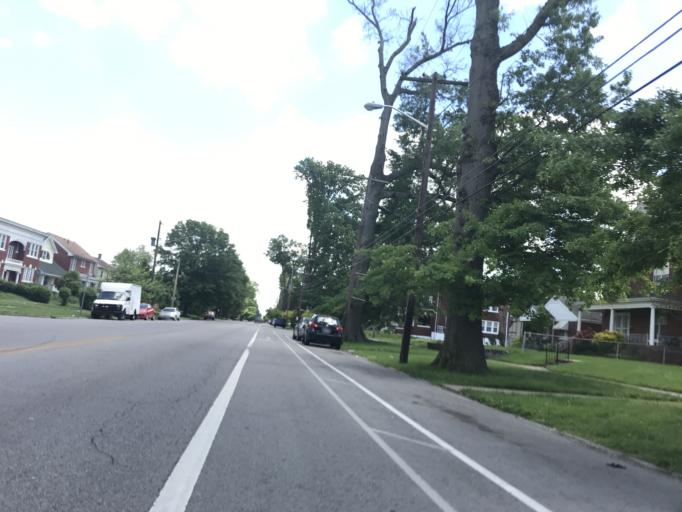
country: US
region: Indiana
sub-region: Floyd County
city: New Albany
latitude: 38.2504
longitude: -85.8244
